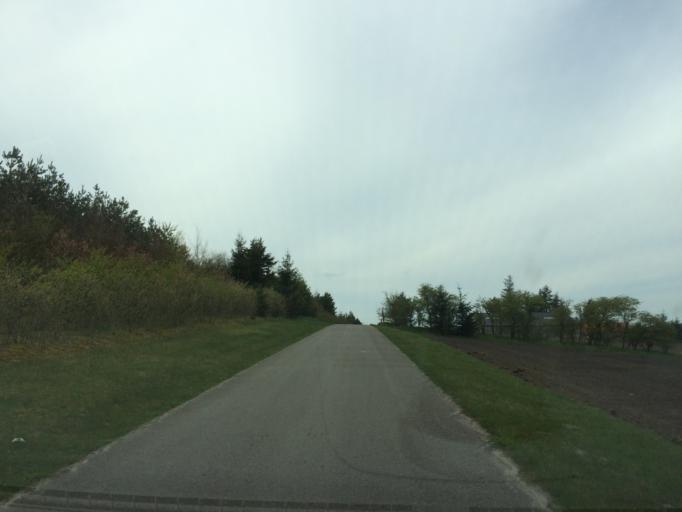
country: DK
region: Central Jutland
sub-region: Holstebro Kommune
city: Ulfborg
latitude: 56.2160
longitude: 8.4845
